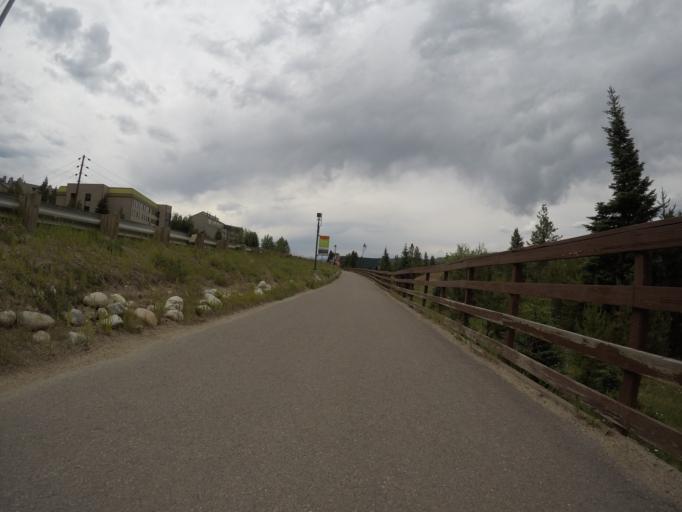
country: US
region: Colorado
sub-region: Grand County
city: Fraser
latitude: 39.9151
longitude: -105.7825
